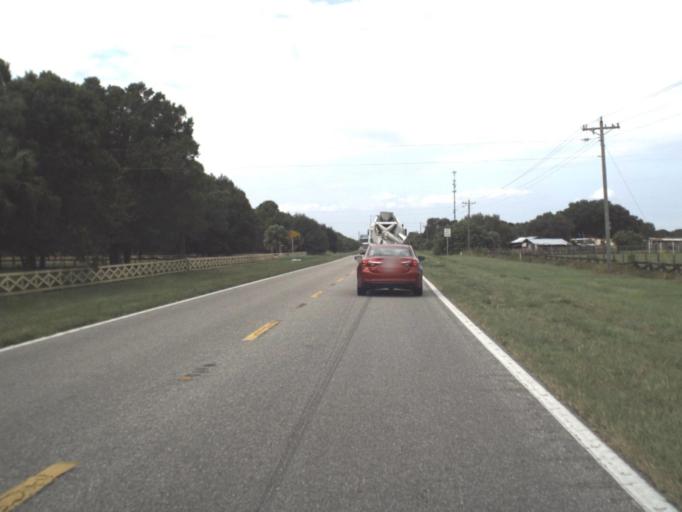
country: US
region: Florida
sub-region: Hendry County
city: Port LaBelle
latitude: 26.7684
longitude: -81.2428
